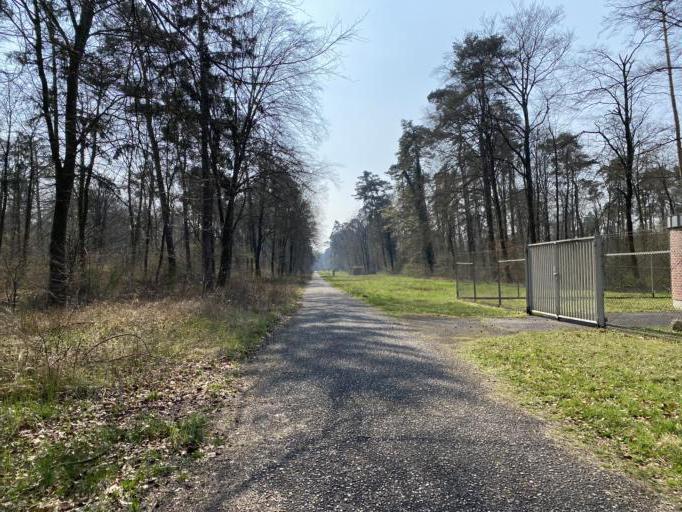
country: DE
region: Baden-Wuerttemberg
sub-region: Karlsruhe Region
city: Karlsruhe
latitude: 49.0493
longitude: 8.4168
